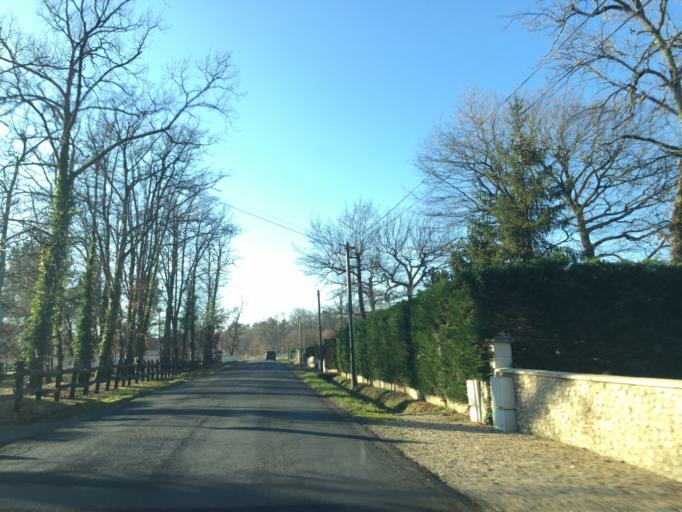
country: FR
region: Aquitaine
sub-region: Departement de la Dordogne
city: Neuvic
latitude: 45.1370
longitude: 0.4832
